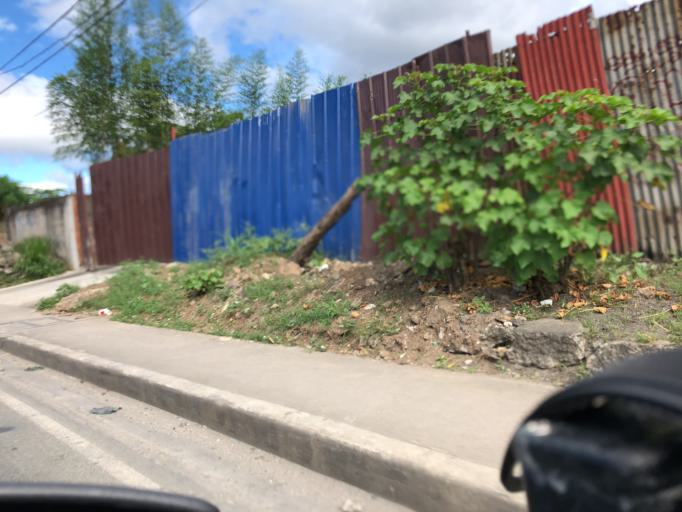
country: PH
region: Calabarzon
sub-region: Province of Rizal
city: San Mateo
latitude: 14.7280
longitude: 121.0612
